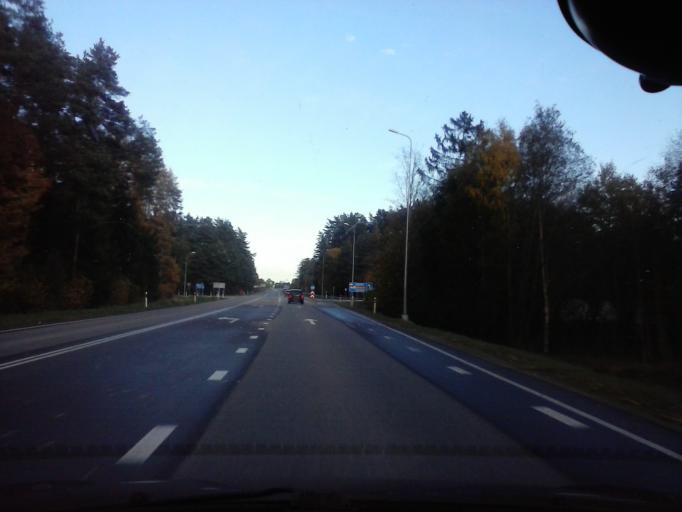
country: EE
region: Laeaene
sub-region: Lihula vald
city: Lihula
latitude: 58.9710
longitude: 23.8839
